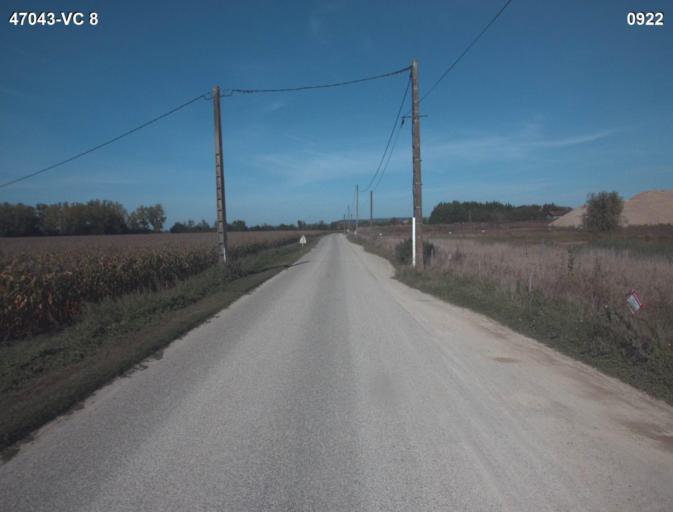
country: FR
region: Aquitaine
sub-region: Departement du Lot-et-Garonne
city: Damazan
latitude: 44.2776
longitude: 0.2917
